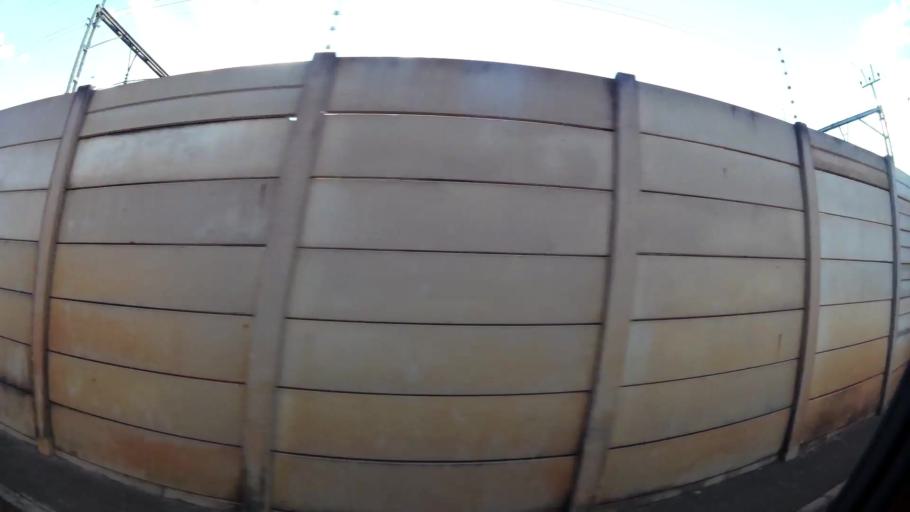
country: ZA
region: North-West
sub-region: Dr Kenneth Kaunda District Municipality
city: Potchefstroom
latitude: -26.6916
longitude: 27.0892
